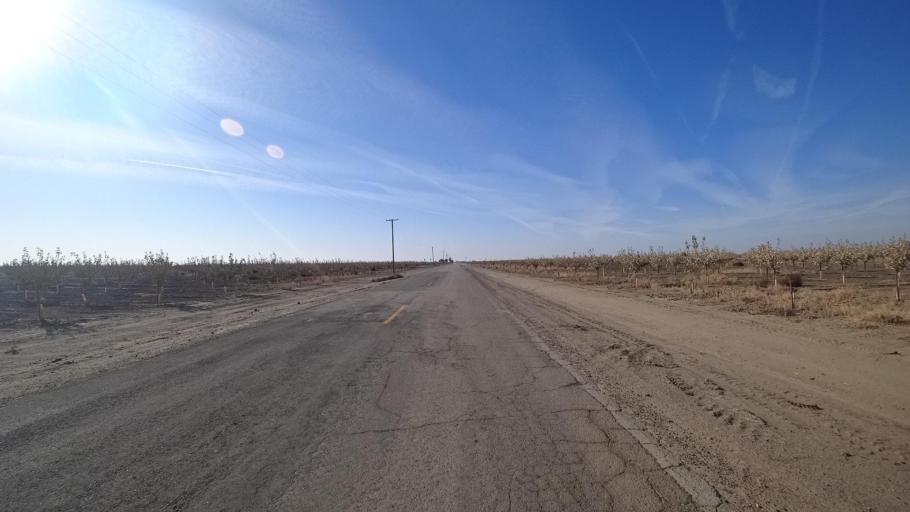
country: US
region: California
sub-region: Kern County
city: Wasco
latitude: 35.7032
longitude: -119.4074
